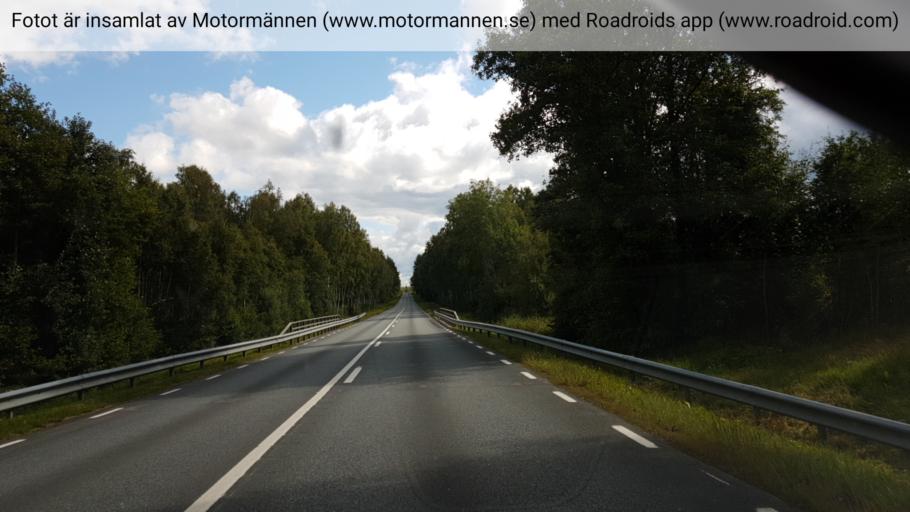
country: SE
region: Joenkoeping
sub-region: Aneby Kommun
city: Hestra
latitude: 57.7781
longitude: 14.5437
